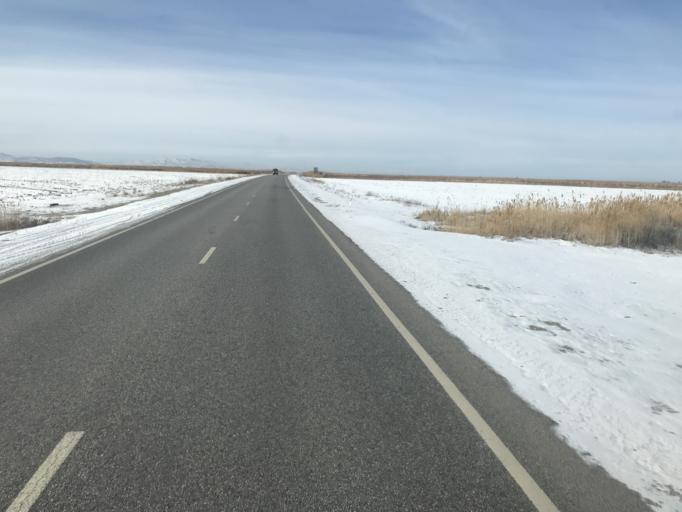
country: KZ
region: Zhambyl
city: Sarykemer
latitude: 43.0379
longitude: 71.4086
